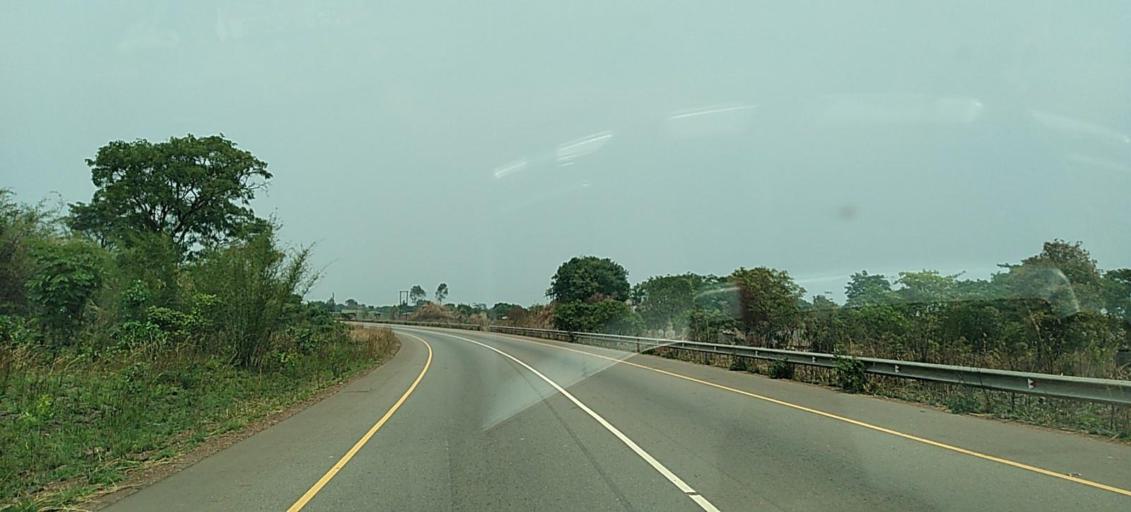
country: ZM
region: Copperbelt
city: Chililabombwe
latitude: -12.5158
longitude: 27.5597
